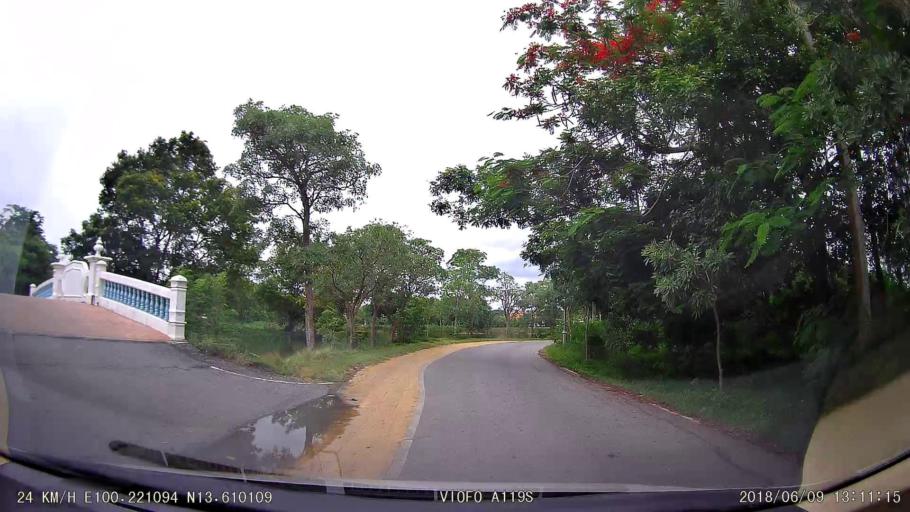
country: TH
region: Samut Sakhon
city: Krathum Baen
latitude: 13.6102
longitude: 100.2208
